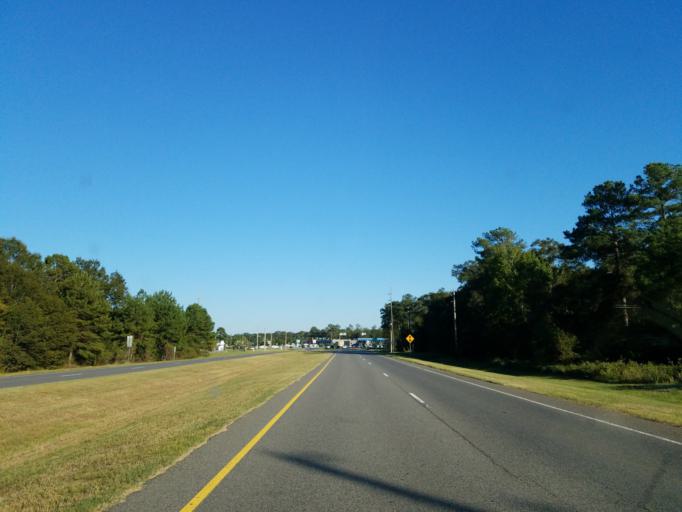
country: US
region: Georgia
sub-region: Lee County
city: Leesburg
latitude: 31.7213
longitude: -84.1759
